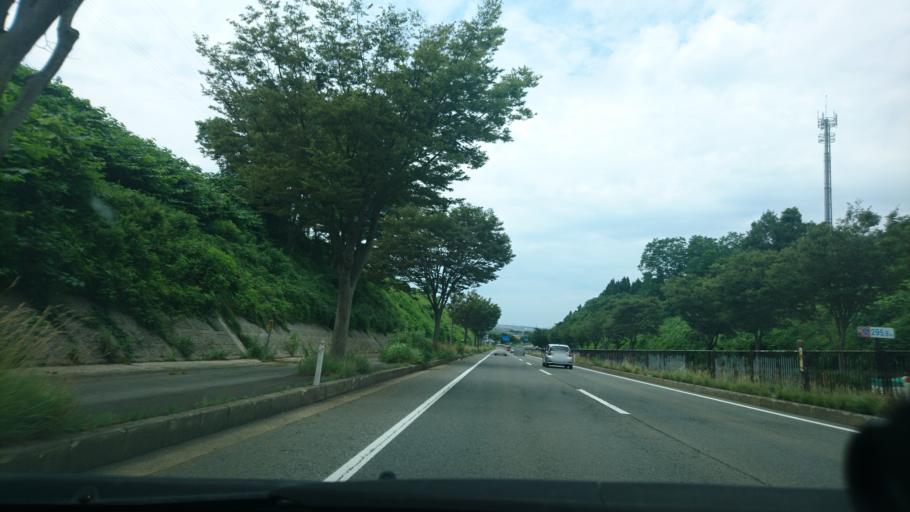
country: JP
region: Akita
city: Akita
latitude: 39.6712
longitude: 140.1590
